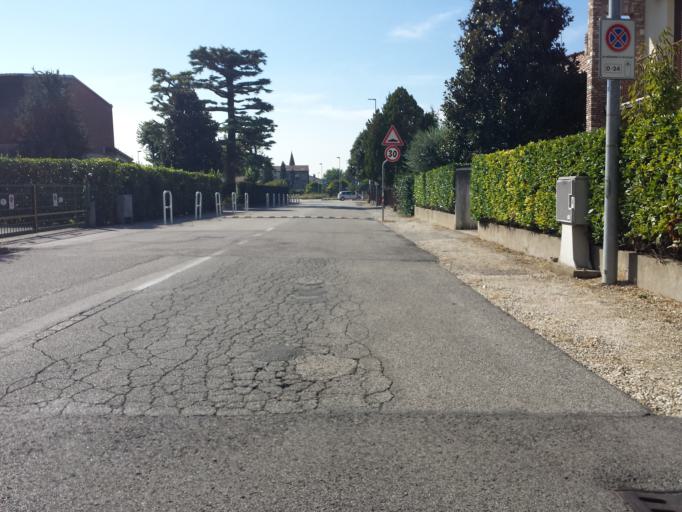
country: IT
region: Veneto
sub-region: Provincia di Vicenza
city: Sandrigo
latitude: 45.6615
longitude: 11.6006
